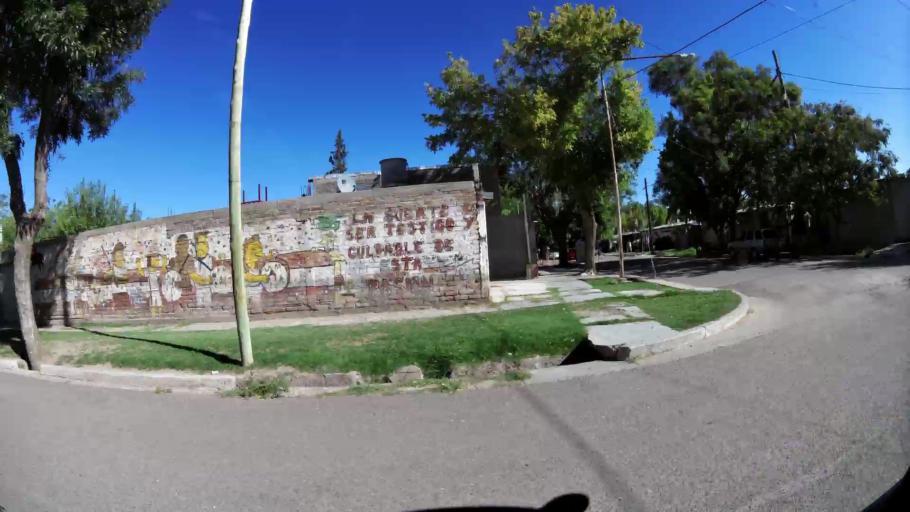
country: AR
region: Mendoza
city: Las Heras
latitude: -32.8458
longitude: -68.8247
